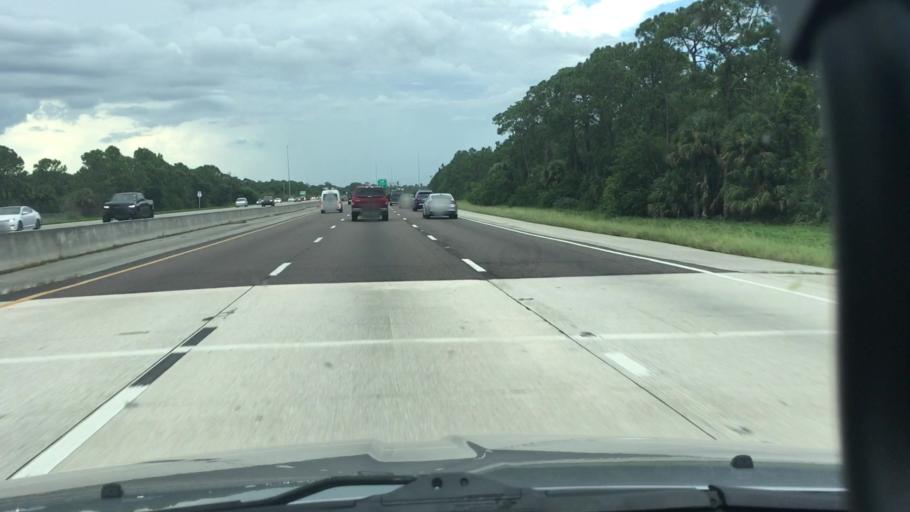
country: US
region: Florida
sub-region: Brevard County
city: Cocoa West
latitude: 28.3994
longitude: -80.8178
